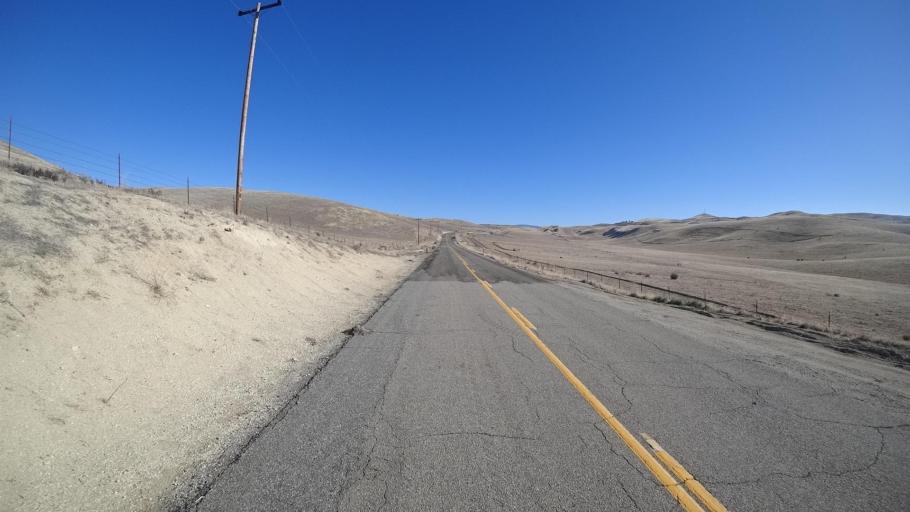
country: US
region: California
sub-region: Kern County
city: Maricopa
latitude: 34.9525
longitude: -119.4278
